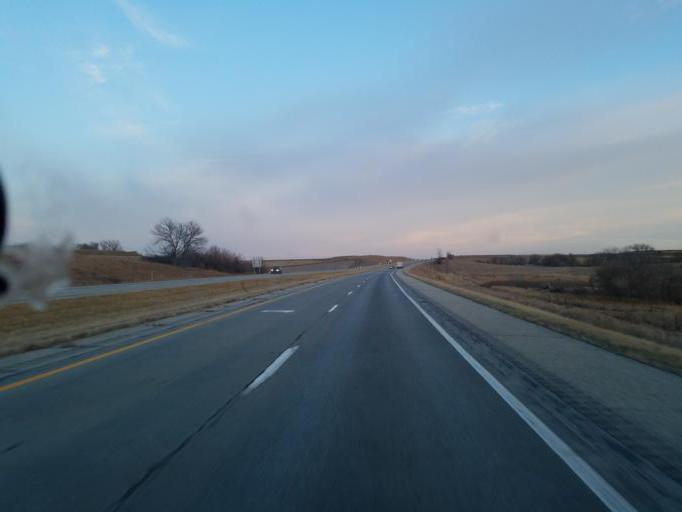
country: US
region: Iowa
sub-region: Pottawattamie County
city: Avoca
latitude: 41.5001
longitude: -95.5245
